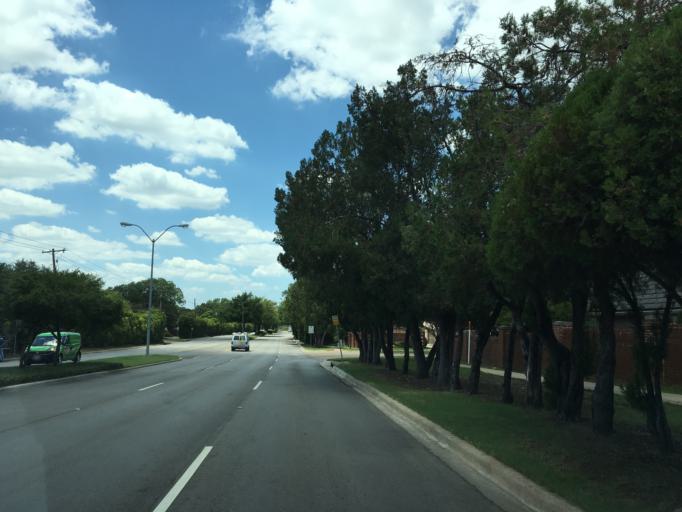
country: US
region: Texas
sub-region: Dallas County
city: Farmers Branch
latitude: 32.9243
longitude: -96.8596
